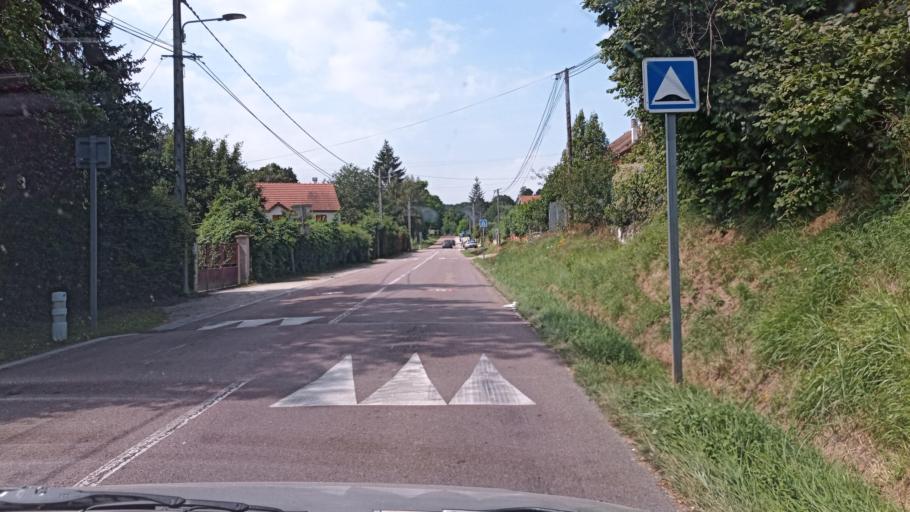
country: FR
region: Bourgogne
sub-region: Departement de l'Yonne
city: Villeneuve-sur-Yonne
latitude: 48.0789
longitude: 3.2824
